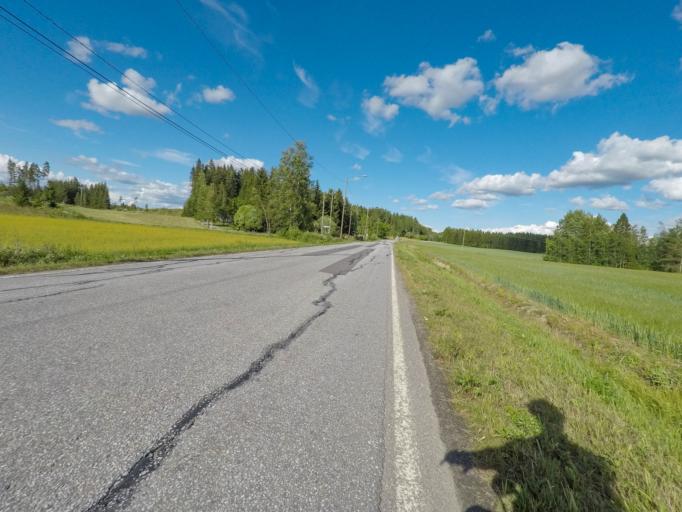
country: FI
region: South Karelia
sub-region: Imatra
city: Imatra
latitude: 61.1286
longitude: 28.7145
